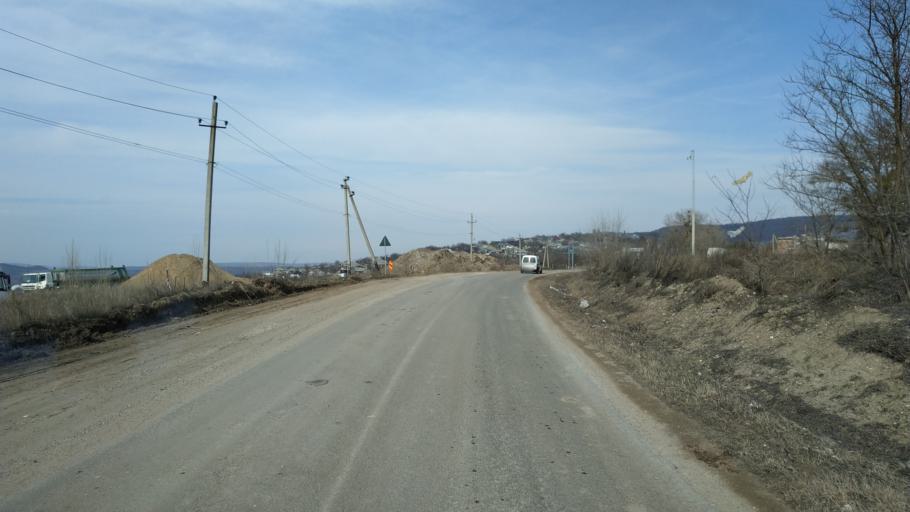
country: MD
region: Nisporeni
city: Nisporeni
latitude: 47.1916
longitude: 28.0670
